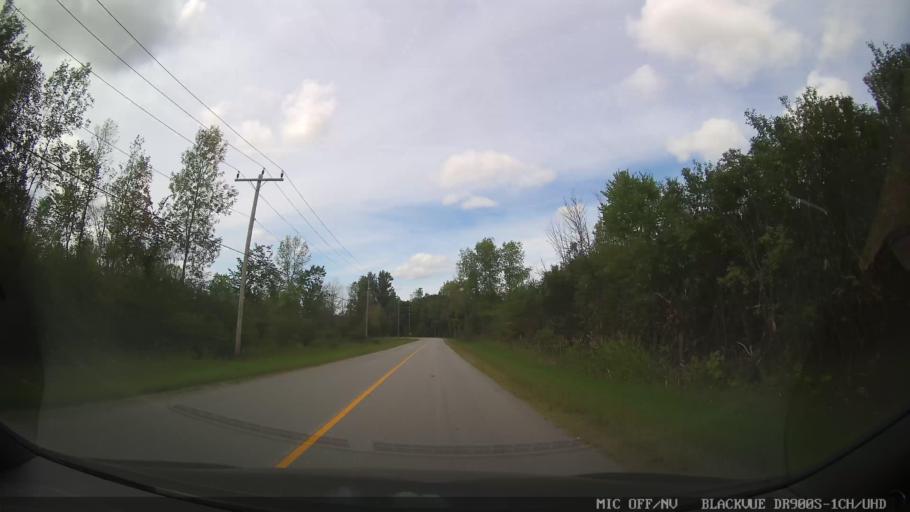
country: CA
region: Ontario
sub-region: Lanark County
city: Smiths Falls
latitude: 44.9235
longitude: -75.8713
